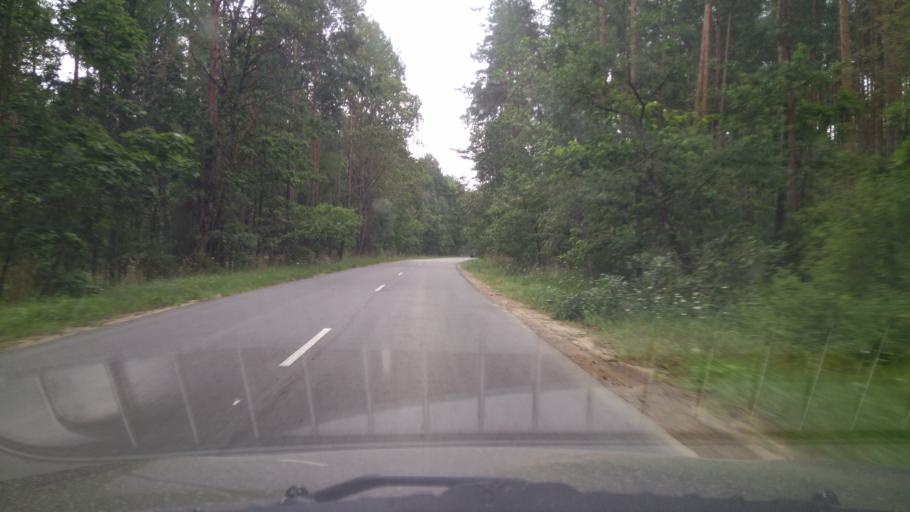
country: BY
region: Brest
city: Nyakhachava
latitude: 52.5995
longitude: 25.0979
